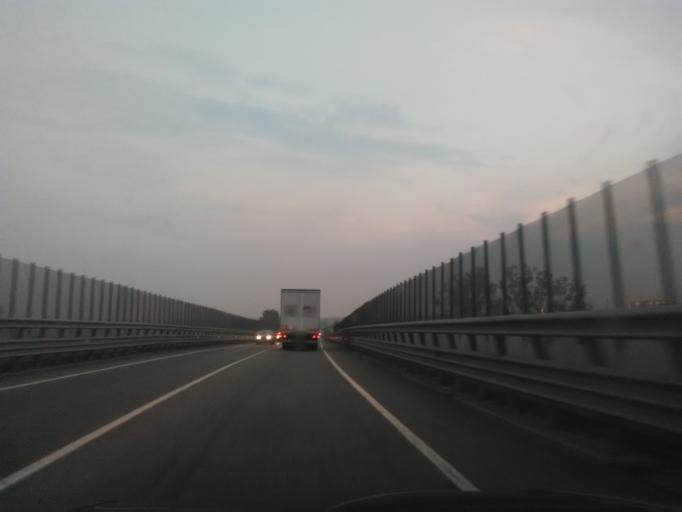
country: IT
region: Piedmont
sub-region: Provincia di Vercelli
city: Carisio
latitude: 45.4349
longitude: 8.2204
